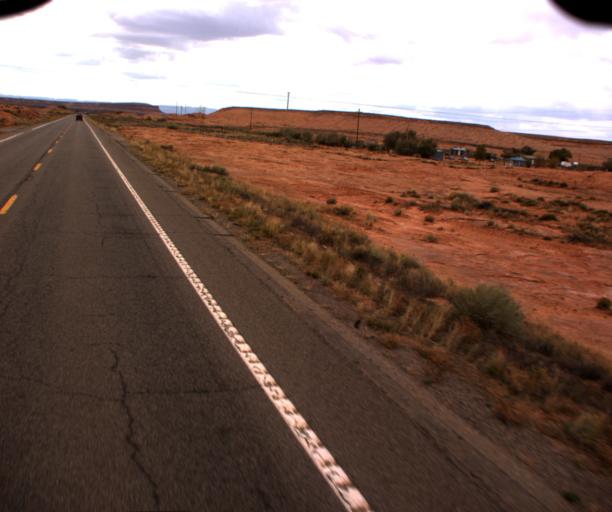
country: US
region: Arizona
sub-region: Navajo County
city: Kayenta
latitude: 36.8271
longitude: -109.8639
